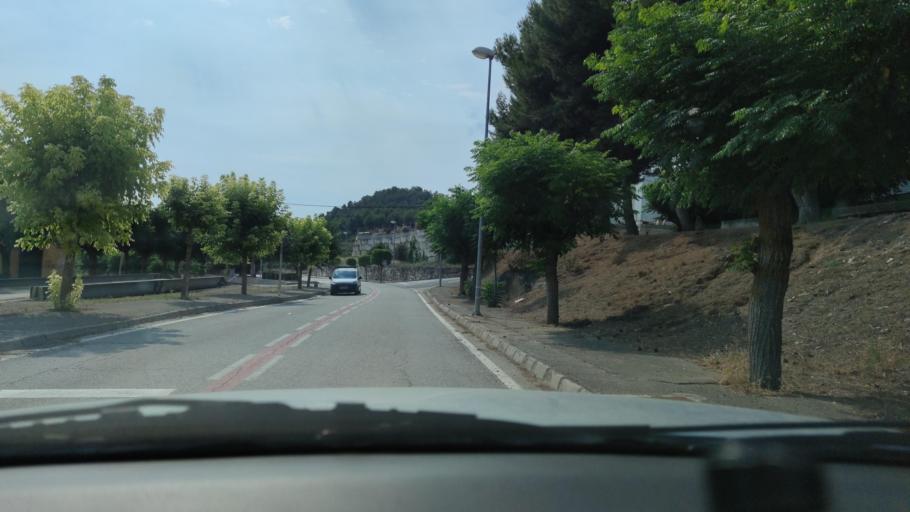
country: ES
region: Catalonia
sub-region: Provincia de Lleida
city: Arbeca
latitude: 41.5003
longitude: 0.9562
